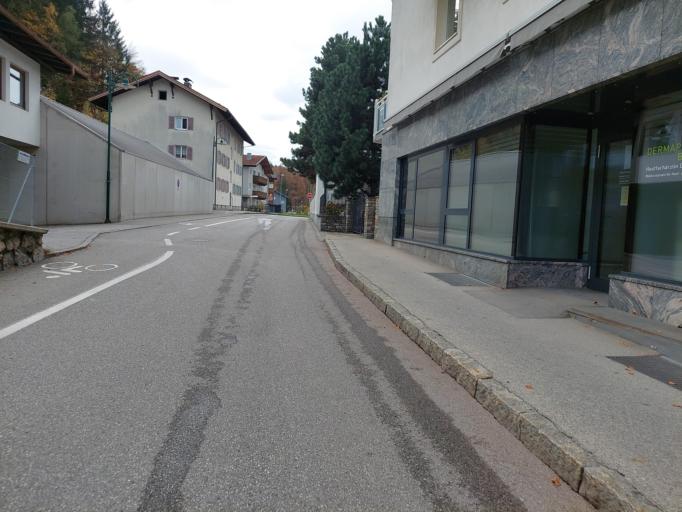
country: AT
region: Tyrol
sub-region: Politischer Bezirk Kufstein
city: Brixlegg
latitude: 47.4275
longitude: 11.8767
